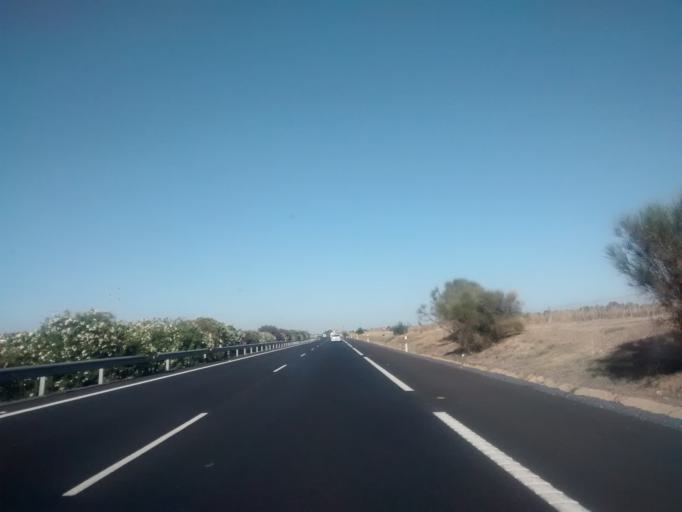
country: ES
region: Andalusia
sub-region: Provincia de Huelva
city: San Juan del Puerto
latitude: 37.3302
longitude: -6.8146
